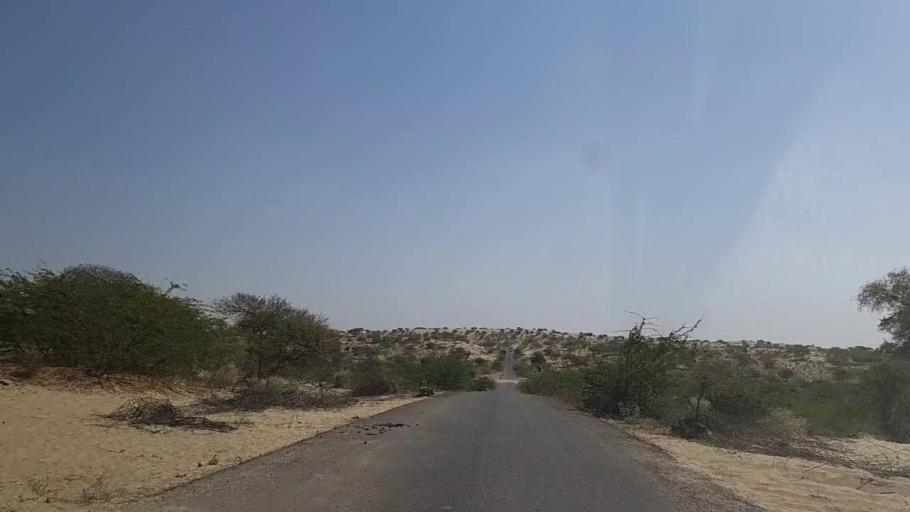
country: PK
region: Sindh
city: Diplo
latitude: 24.4870
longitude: 69.4466
